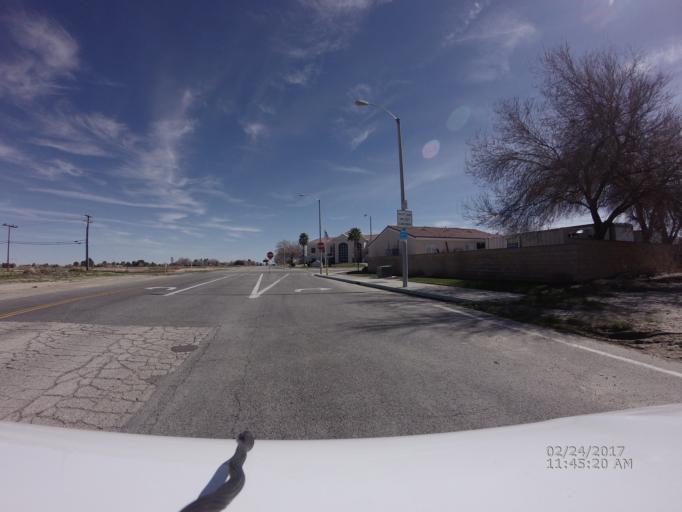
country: US
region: California
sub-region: Los Angeles County
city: Lancaster
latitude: 34.6973
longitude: -118.0598
